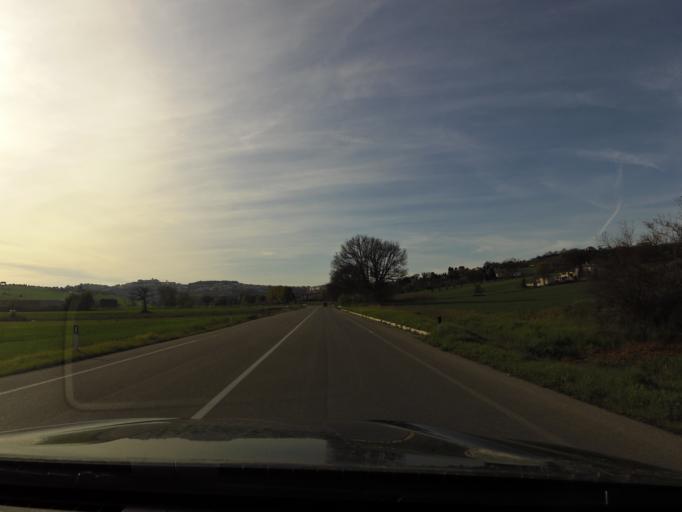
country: IT
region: The Marches
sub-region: Provincia di Ancona
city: Villa Musone
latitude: 43.4569
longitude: 13.5892
